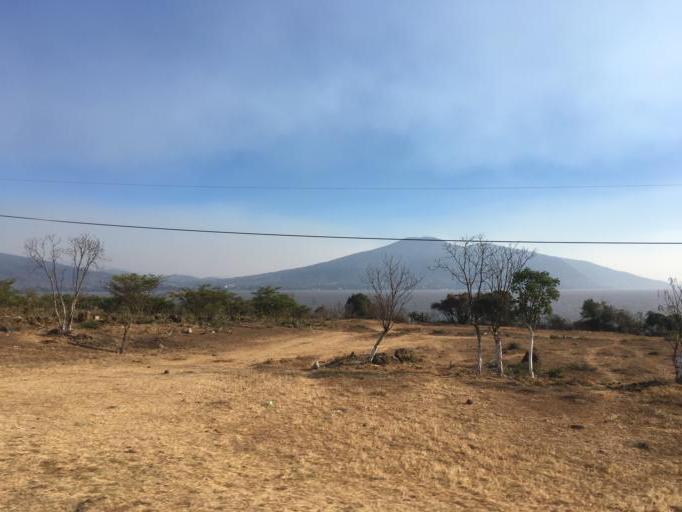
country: MX
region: Michoacan
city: Santa Fe de la Laguna
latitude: 19.6722
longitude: -101.5736
